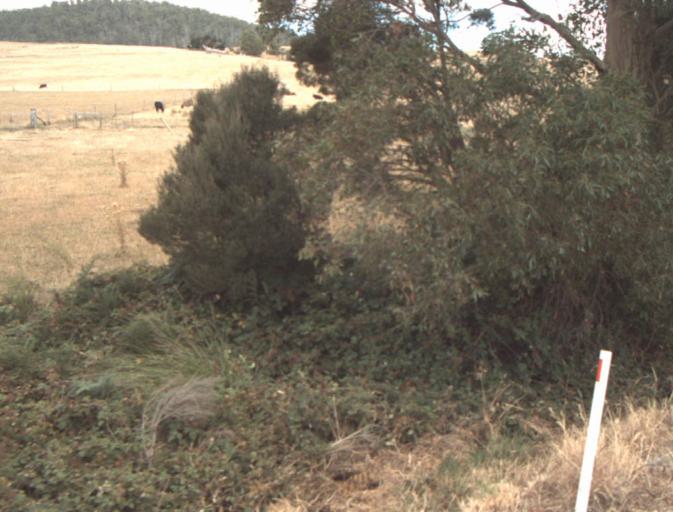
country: AU
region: Tasmania
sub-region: Launceston
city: Mayfield
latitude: -41.2042
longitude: 147.0781
